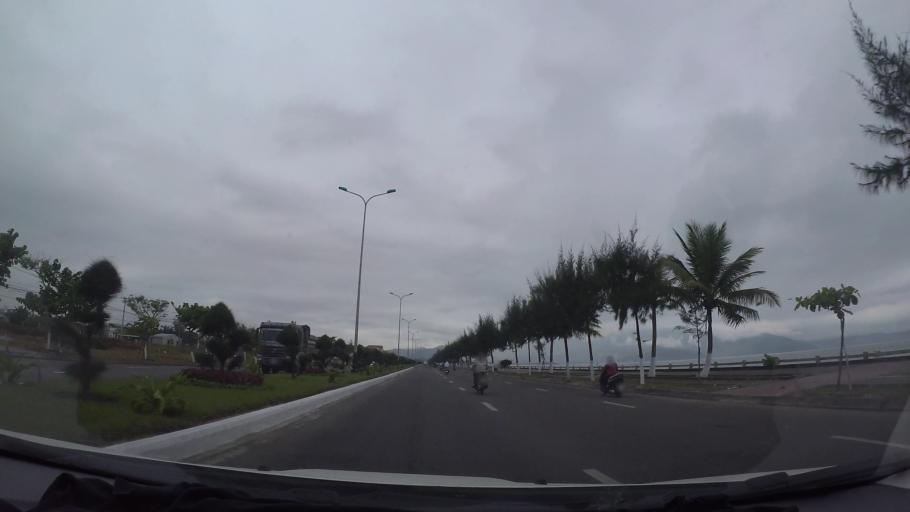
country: VN
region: Da Nang
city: Lien Chieu
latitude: 16.0860
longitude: 108.1585
